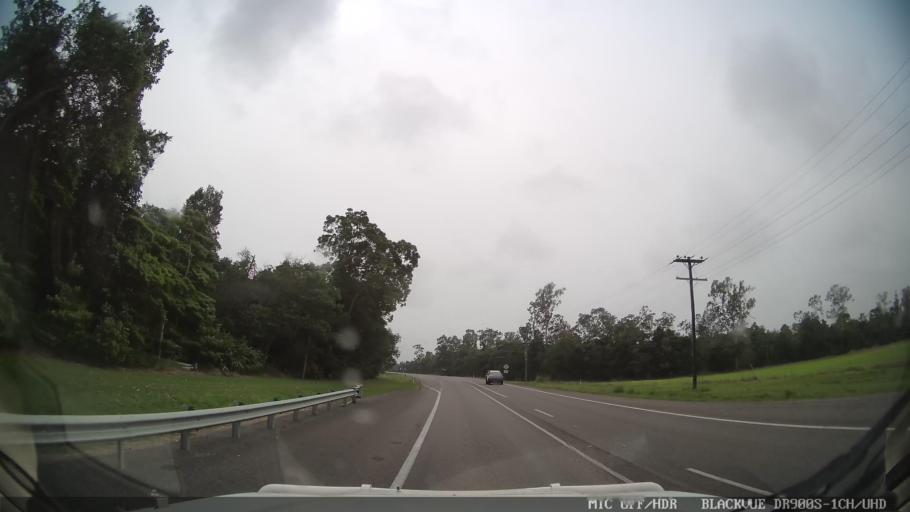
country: AU
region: Queensland
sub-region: Hinchinbrook
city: Ingham
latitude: -18.1202
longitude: 145.9132
